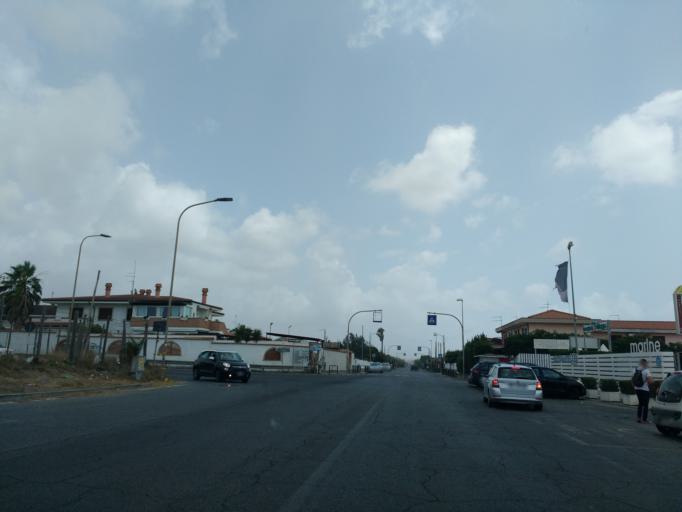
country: IT
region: Latium
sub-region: Citta metropolitana di Roma Capitale
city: Torvaianica
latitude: 41.6568
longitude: 12.4168
